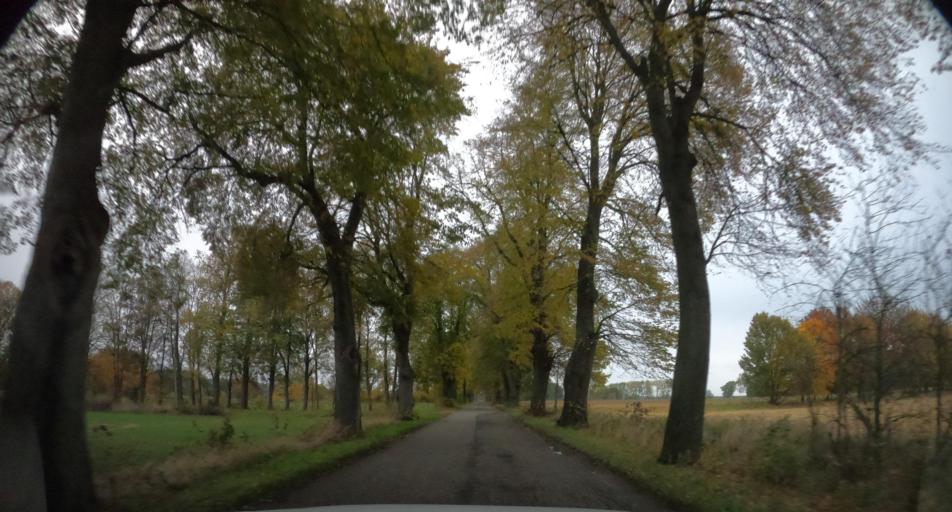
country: PL
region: West Pomeranian Voivodeship
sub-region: Powiat kamienski
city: Wolin
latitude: 53.9056
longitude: 14.6216
